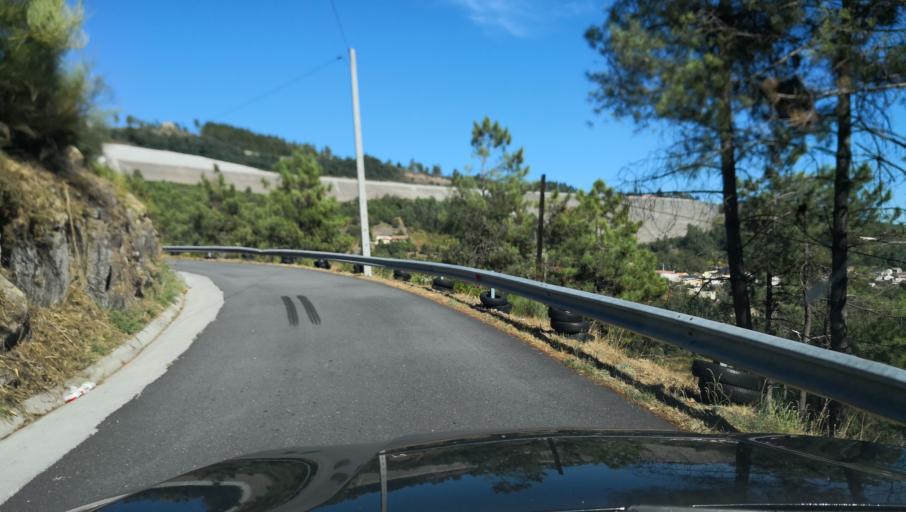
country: PT
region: Vila Real
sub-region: Santa Marta de Penaguiao
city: Santa Marta de Penaguiao
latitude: 41.2747
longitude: -7.8689
